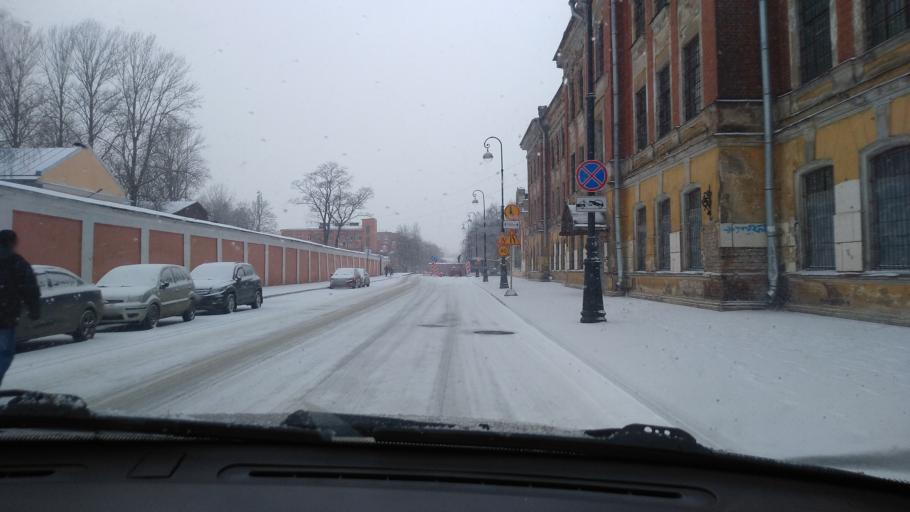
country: RU
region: St.-Petersburg
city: Kronshtadt
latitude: 59.9862
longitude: 29.7827
